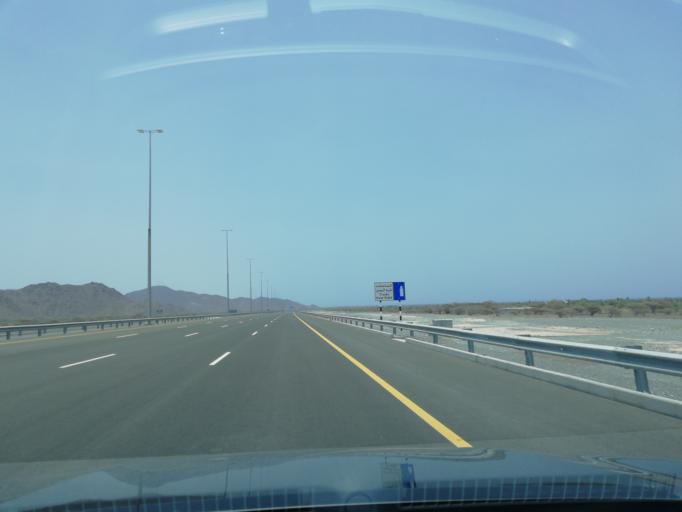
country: AE
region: Al Fujayrah
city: Al Fujayrah
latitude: 24.9320
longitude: 56.3565
